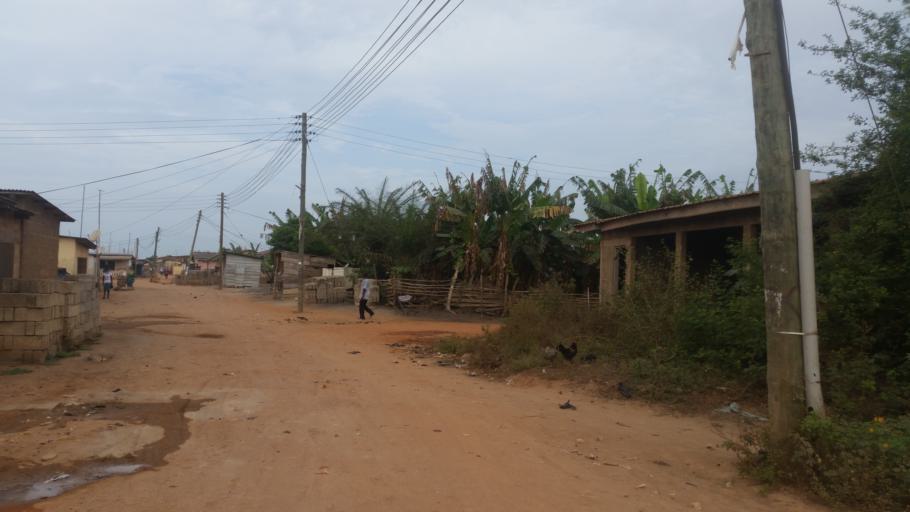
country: GH
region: Central
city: Cape Coast
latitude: 5.1251
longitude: -1.3014
